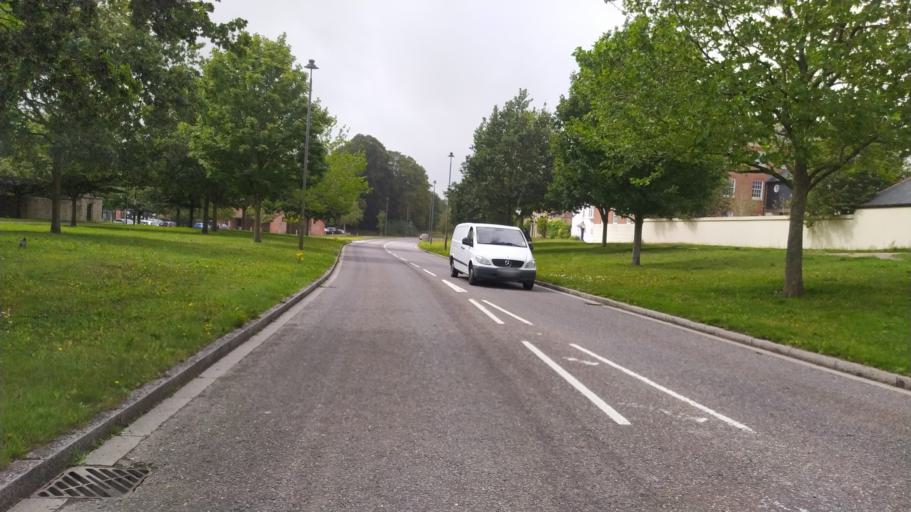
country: GB
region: England
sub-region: Dorset
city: Dorchester
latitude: 50.7116
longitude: -2.4600
